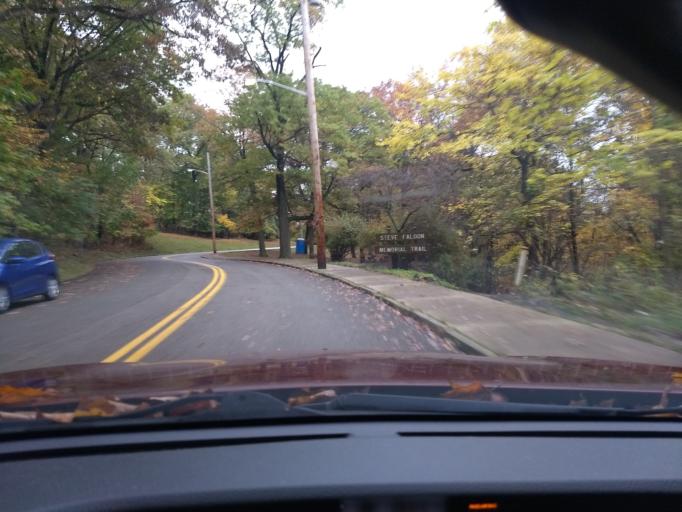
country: US
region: Pennsylvania
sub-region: Allegheny County
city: Bloomfield
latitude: 40.4388
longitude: -79.9437
